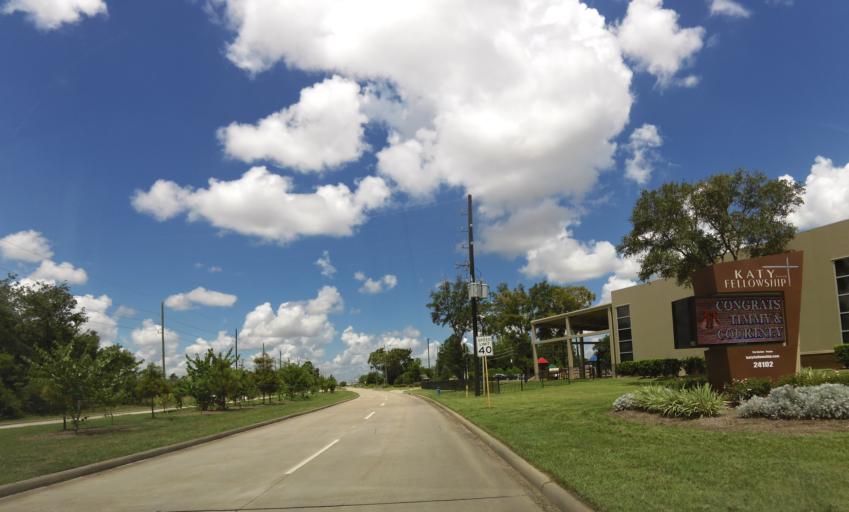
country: US
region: Texas
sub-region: Harris County
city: Katy
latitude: 29.7737
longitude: -95.7909
